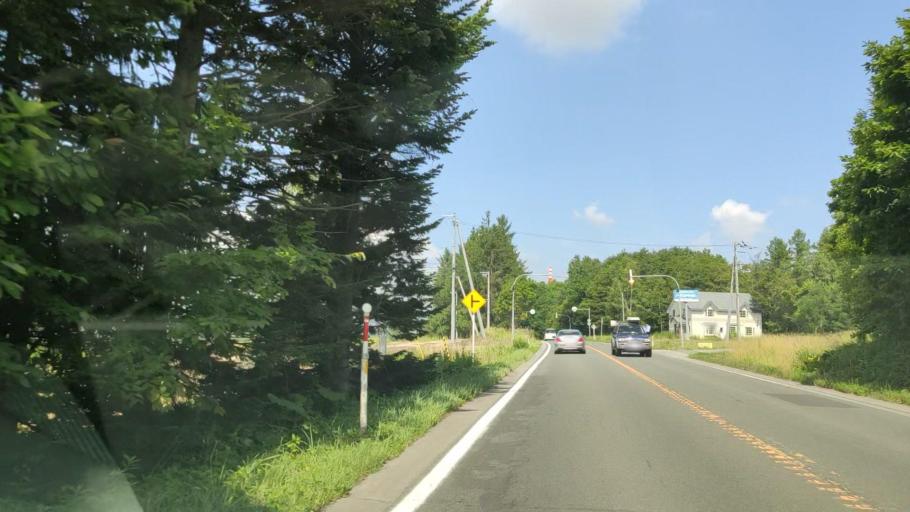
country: JP
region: Hokkaido
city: Shimo-furano
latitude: 43.5095
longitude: 142.4542
